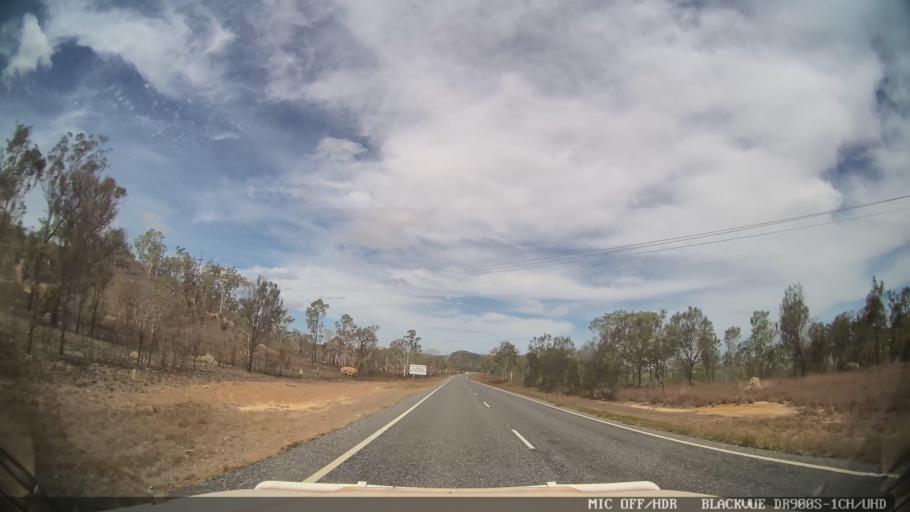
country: AU
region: Queensland
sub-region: Tablelands
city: Mareeba
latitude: -16.7839
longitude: 145.3476
